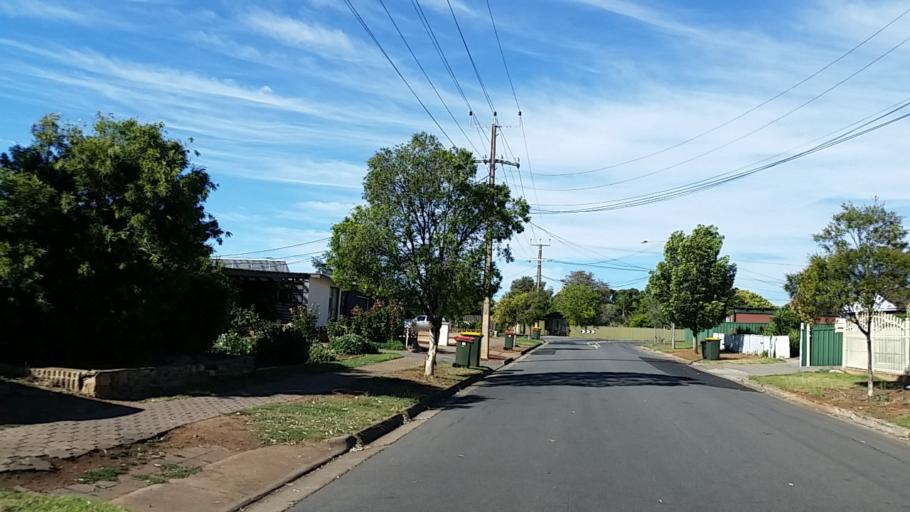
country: AU
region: South Australia
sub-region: Salisbury
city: Salisbury
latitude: -34.7748
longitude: 138.6585
